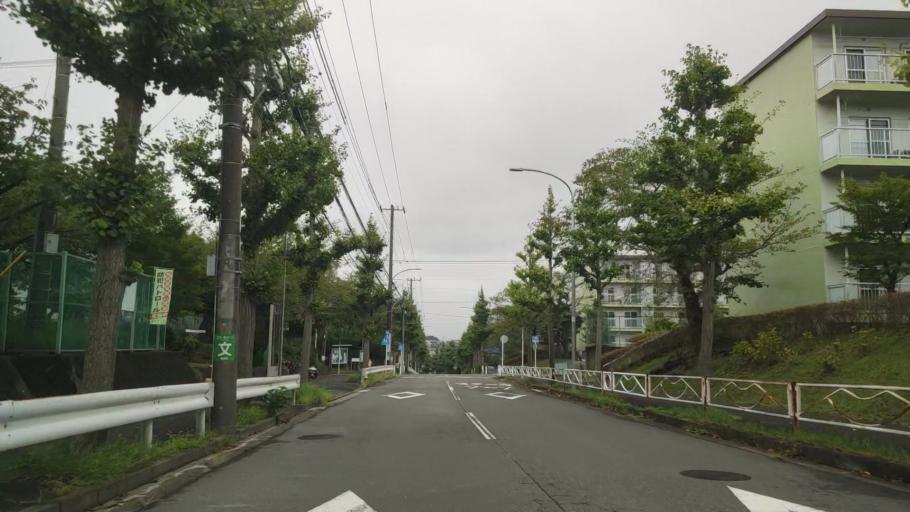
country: JP
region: Kanagawa
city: Zushi
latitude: 35.3690
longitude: 139.6096
